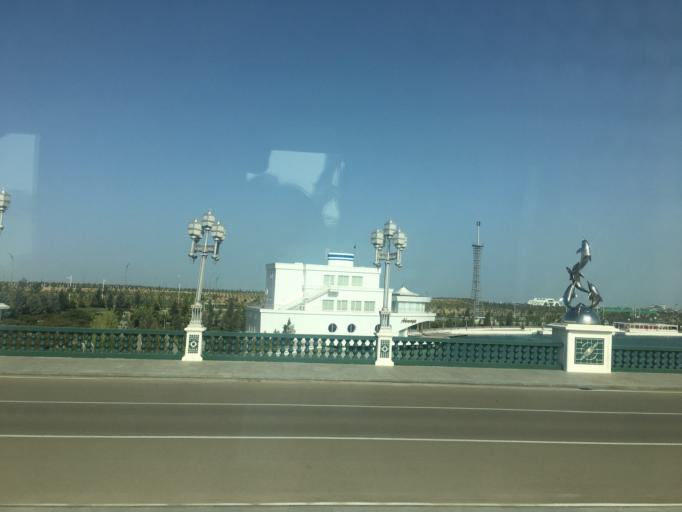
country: TM
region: Balkan
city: Turkmenbasy
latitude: 39.9539
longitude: 52.8641
